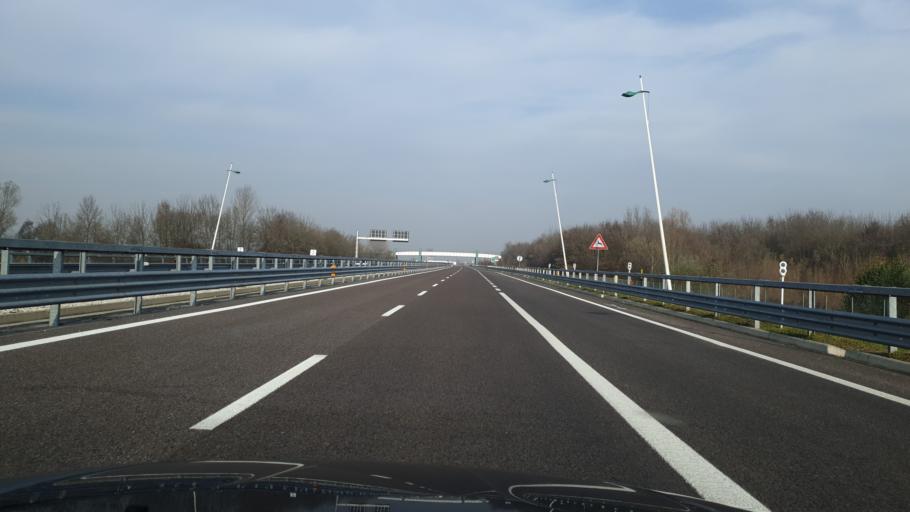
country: IT
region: Veneto
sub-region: Provincia di Padova
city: Piacenza d'Adige
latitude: 45.1318
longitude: 11.5307
